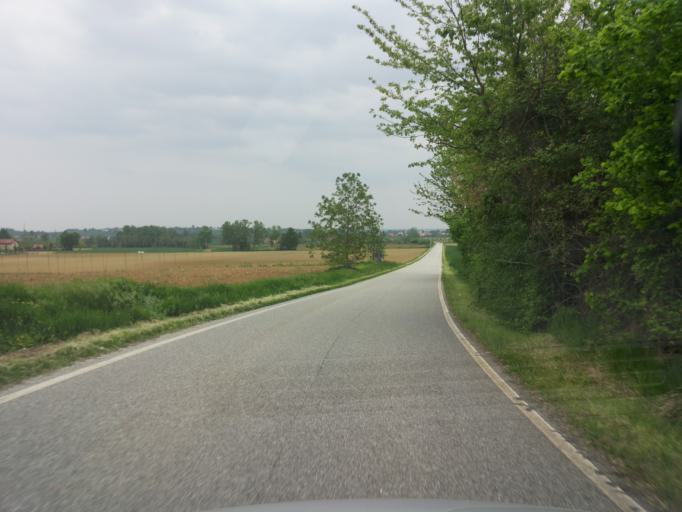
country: IT
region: Piedmont
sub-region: Provincia di Alessandria
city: Mirabello Monferrato
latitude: 45.0181
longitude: 8.5125
